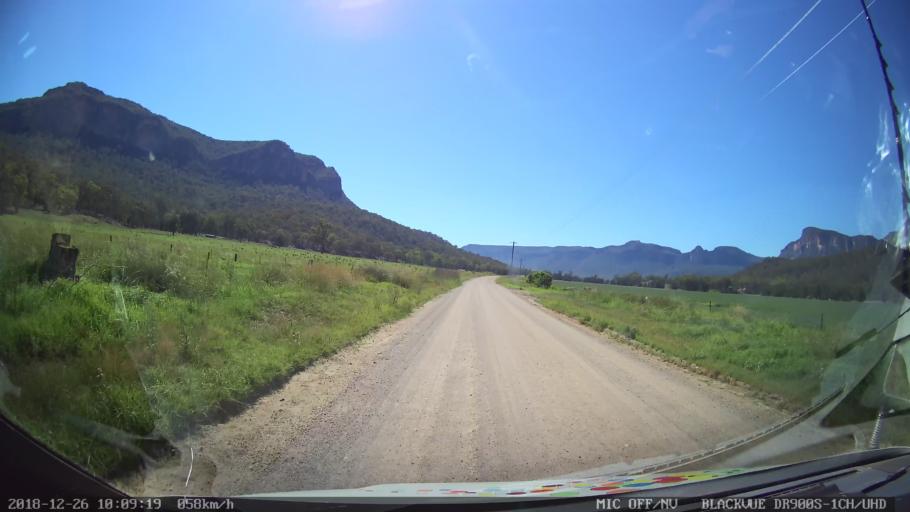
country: AU
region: New South Wales
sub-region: Lithgow
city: Portland
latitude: -33.1020
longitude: 150.2371
